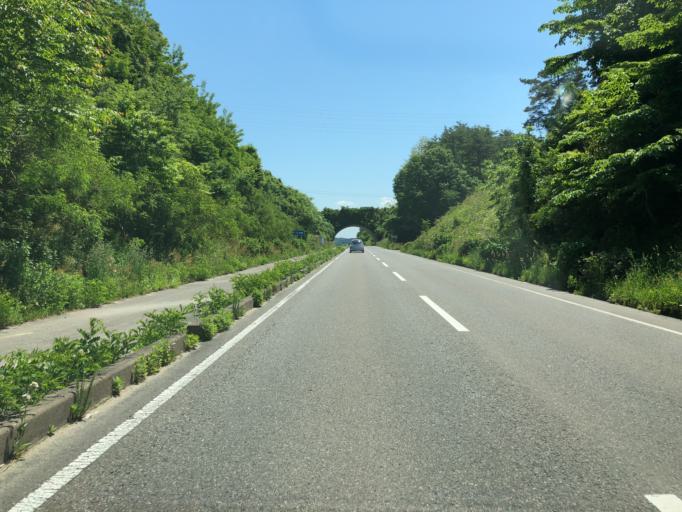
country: JP
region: Fukushima
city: Motomiya
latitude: 37.5309
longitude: 140.4273
